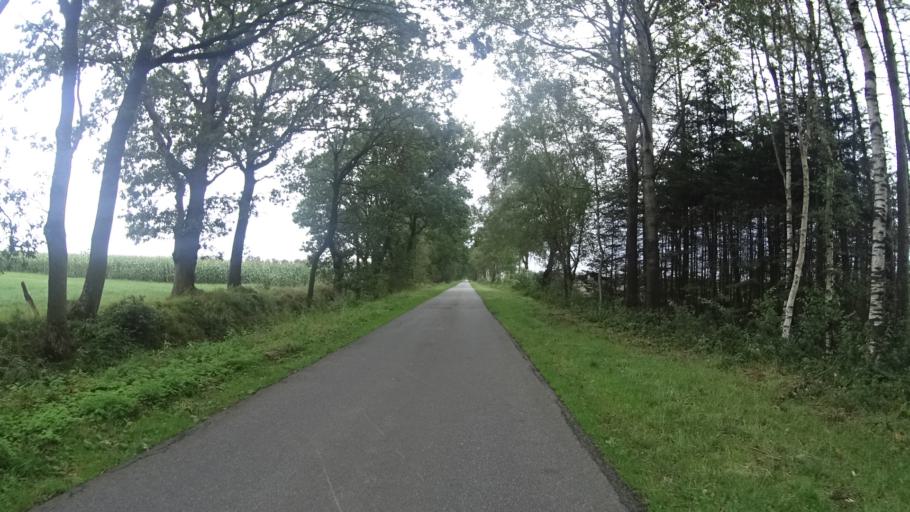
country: DE
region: Lower Saxony
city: Lintig
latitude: 53.6327
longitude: 8.9113
